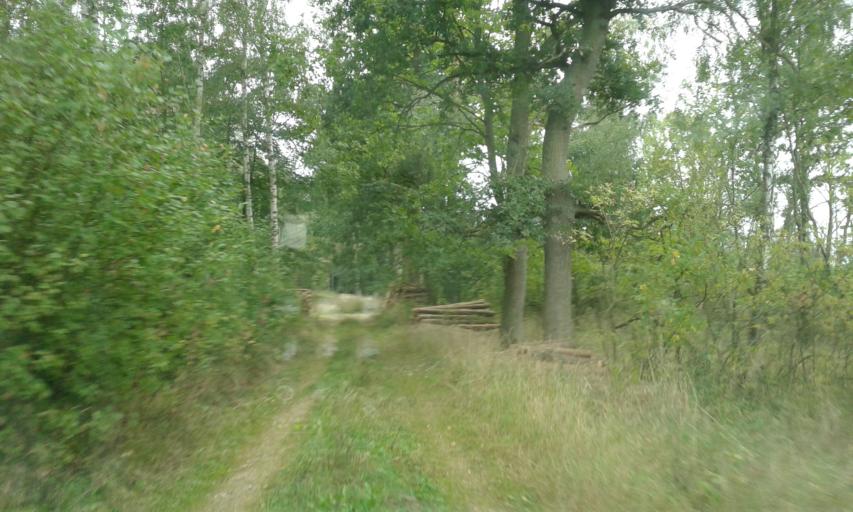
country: PL
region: West Pomeranian Voivodeship
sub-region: Powiat stargardzki
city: Dolice
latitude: 53.1728
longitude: 15.1379
